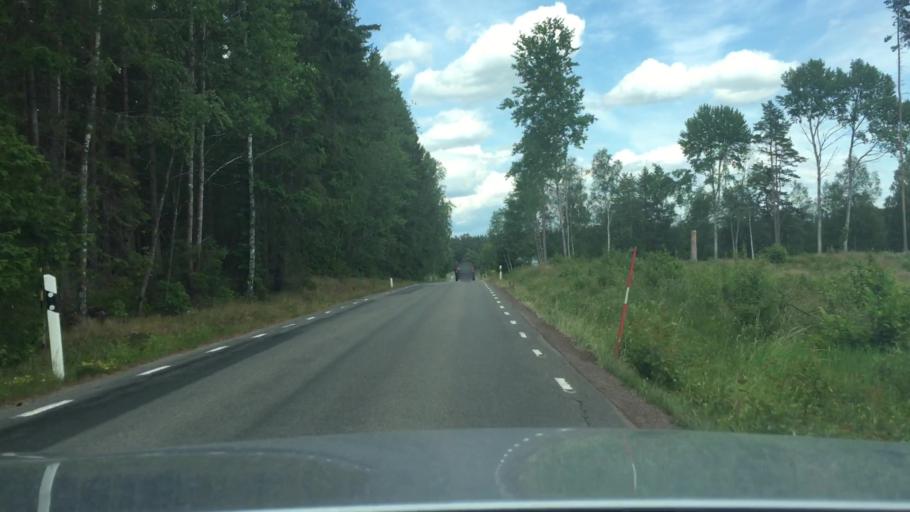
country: SE
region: Vaestra Goetaland
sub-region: Tidaholms Kommun
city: Tidaholm
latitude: 58.2053
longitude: 13.9813
